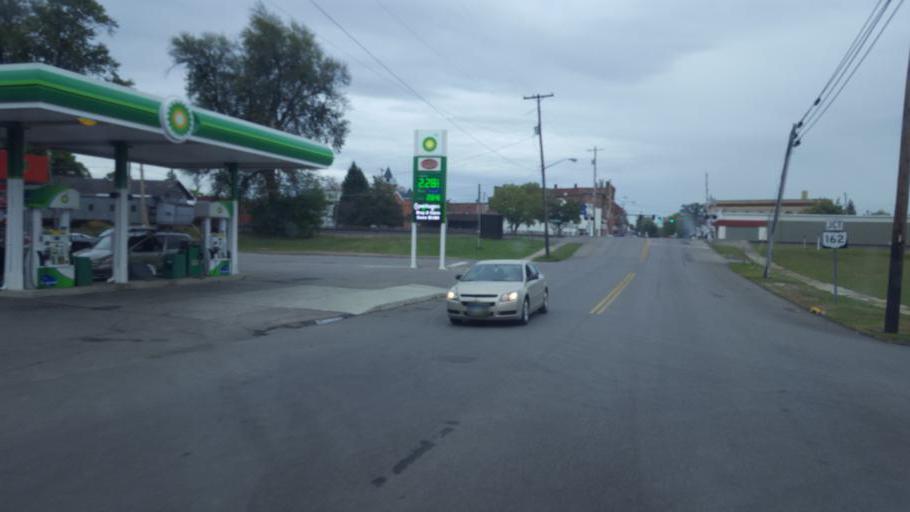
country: US
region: Ohio
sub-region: Huron County
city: New London
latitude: 41.0868
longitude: -82.3999
